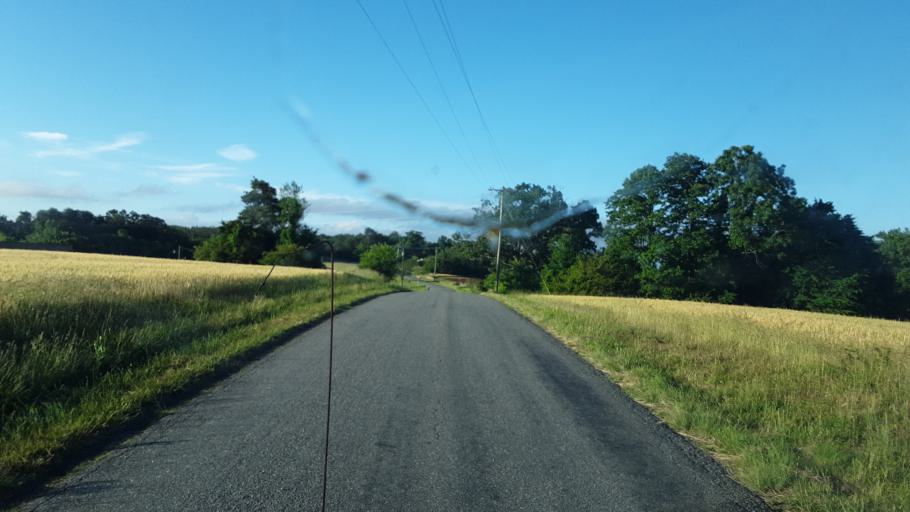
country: US
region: Virginia
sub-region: Pittsylvania County
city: Chatham
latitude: 36.8426
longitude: -79.4462
